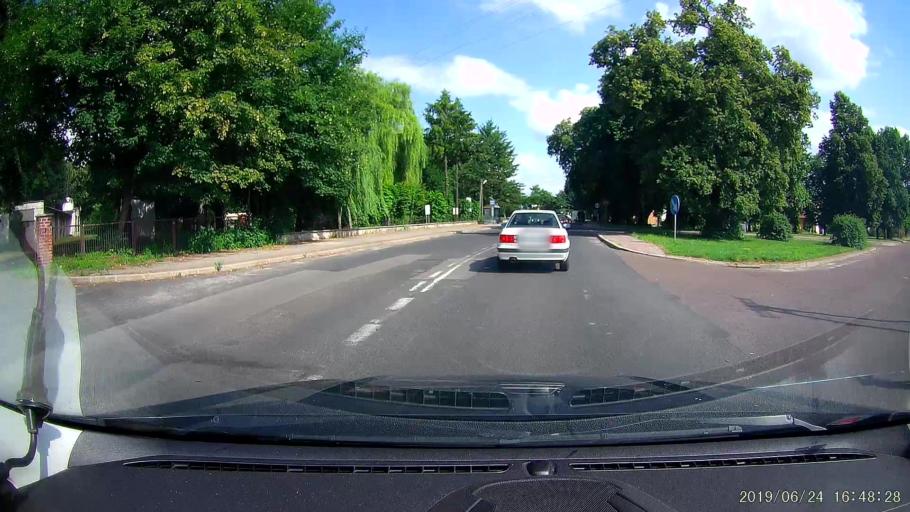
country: PL
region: Lublin Voivodeship
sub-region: Powiat tomaszowski
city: Laszczow
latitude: 50.5320
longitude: 23.7153
